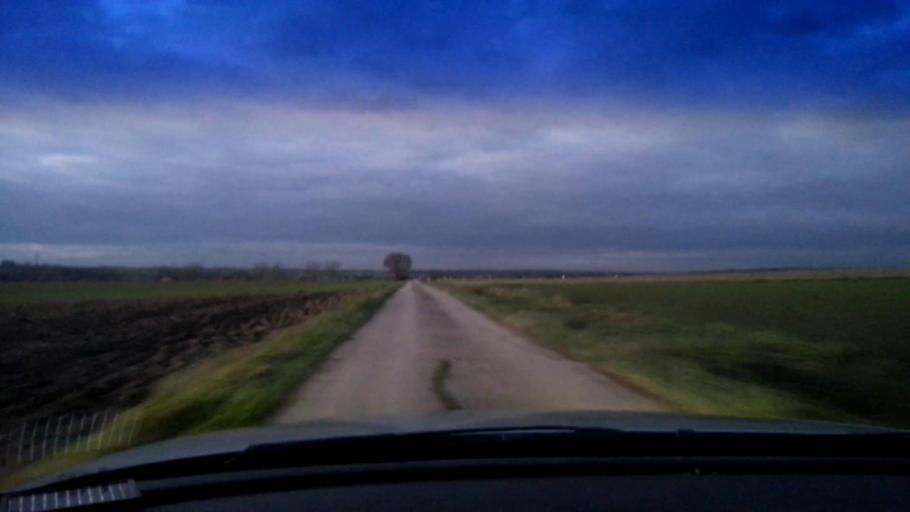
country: DE
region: Bavaria
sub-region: Upper Franconia
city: Schesslitz
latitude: 49.9519
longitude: 11.0070
